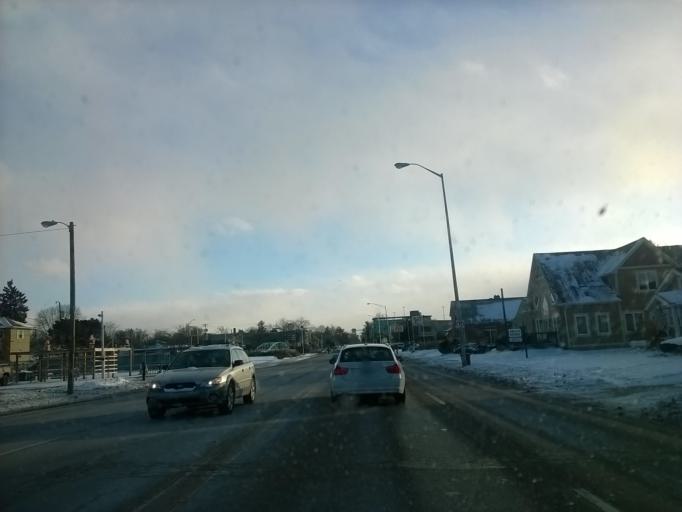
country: US
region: Indiana
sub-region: Marion County
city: Broad Ripple
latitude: 39.8718
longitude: -86.1463
